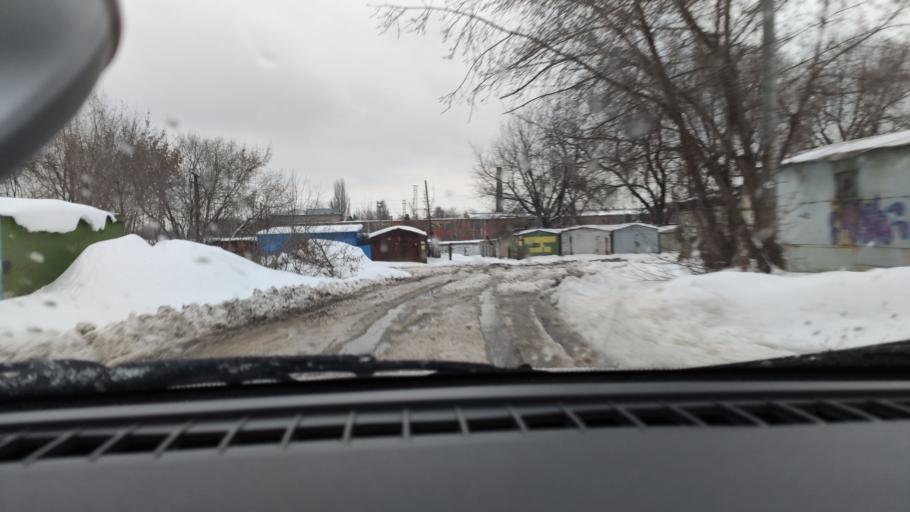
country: RU
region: Samara
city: Samara
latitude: 53.2108
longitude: 50.2597
